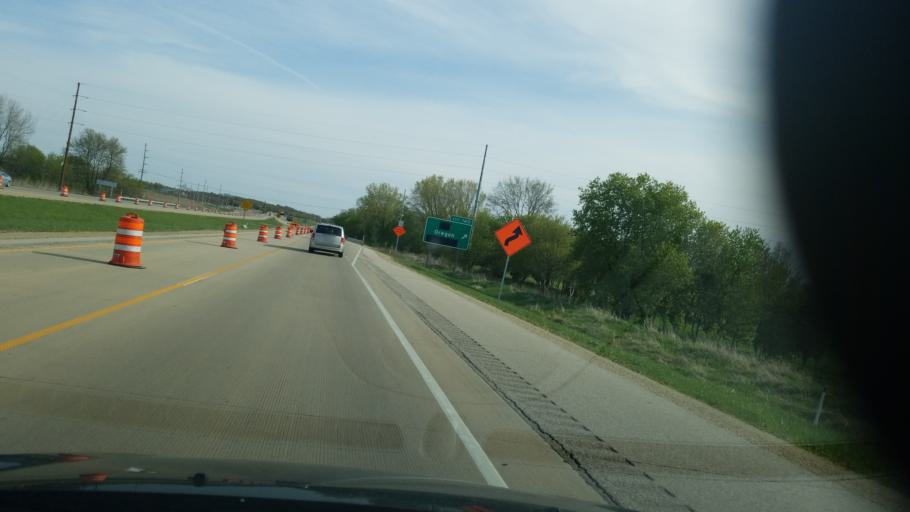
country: US
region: Wisconsin
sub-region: Dane County
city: Oregon
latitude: 42.9247
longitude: -89.3694
